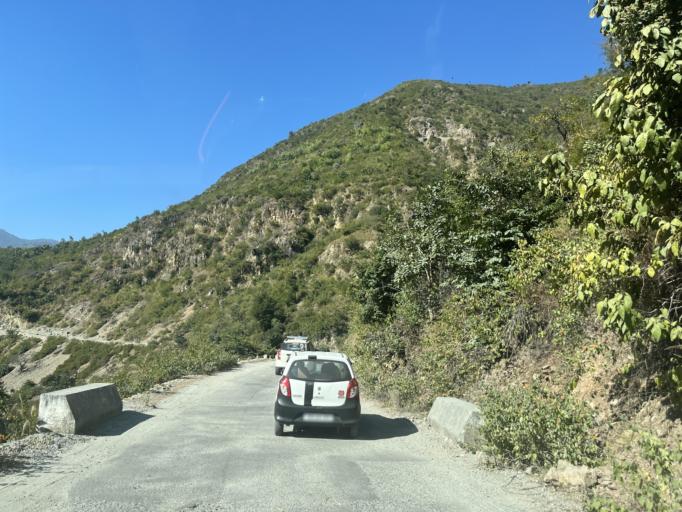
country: IN
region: Uttarakhand
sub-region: Naini Tal
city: Naini Tal
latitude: 29.5109
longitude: 79.4688
